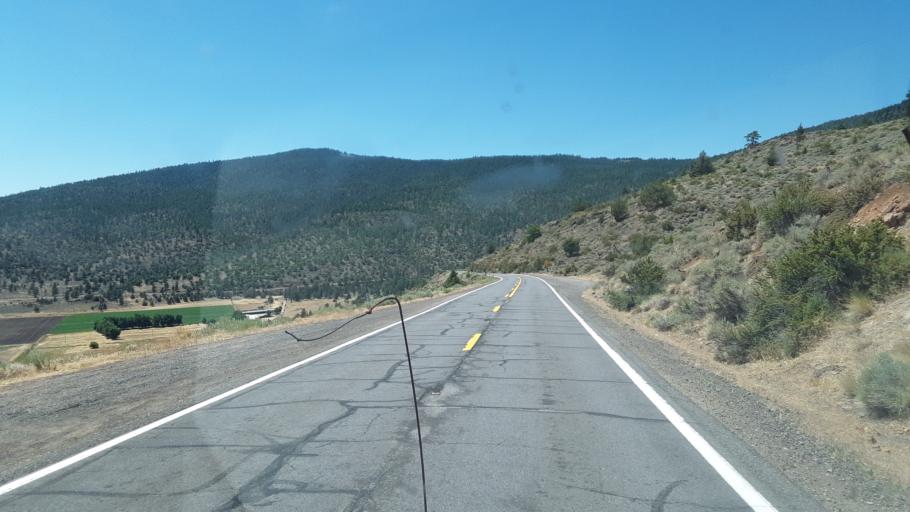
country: US
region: California
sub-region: Lassen County
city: Susanville
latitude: 40.4603
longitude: -120.5963
